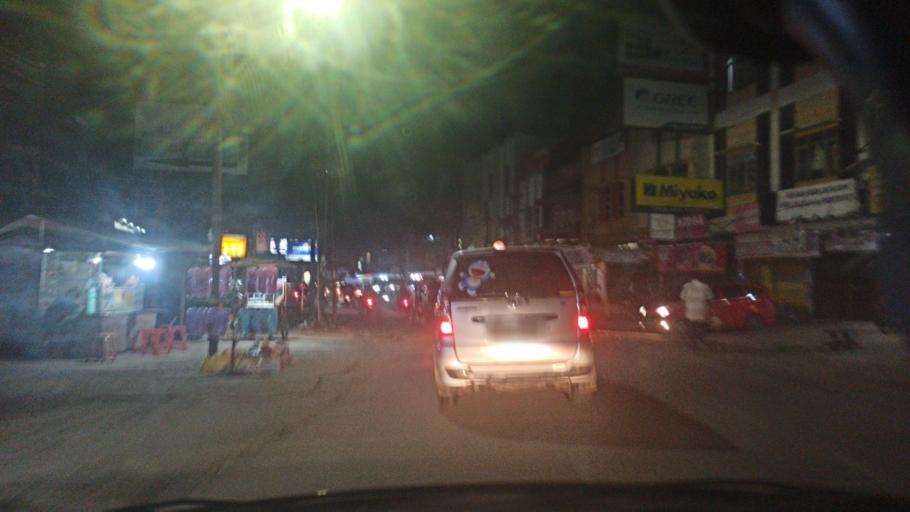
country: ID
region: South Sumatra
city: Palembang
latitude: -2.9229
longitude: 104.7823
